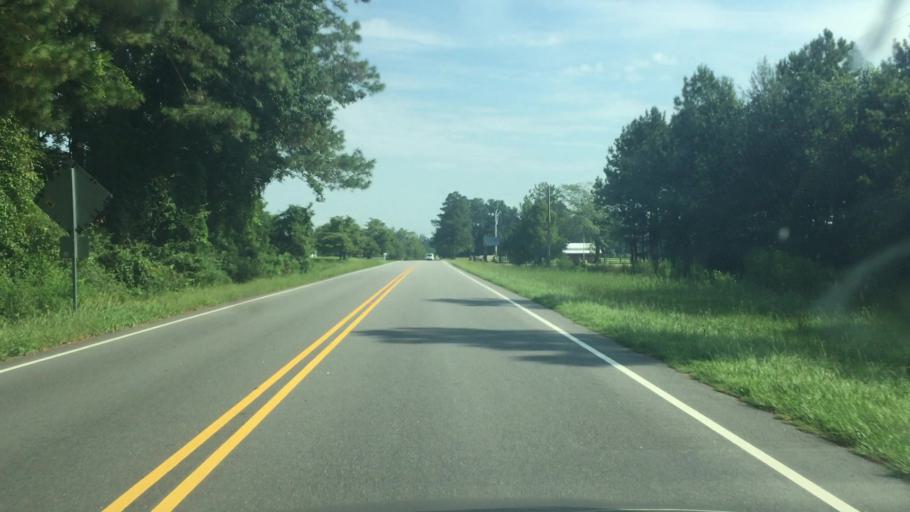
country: US
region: North Carolina
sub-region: Columbus County
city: Chadbourn
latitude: 34.2504
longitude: -78.8190
